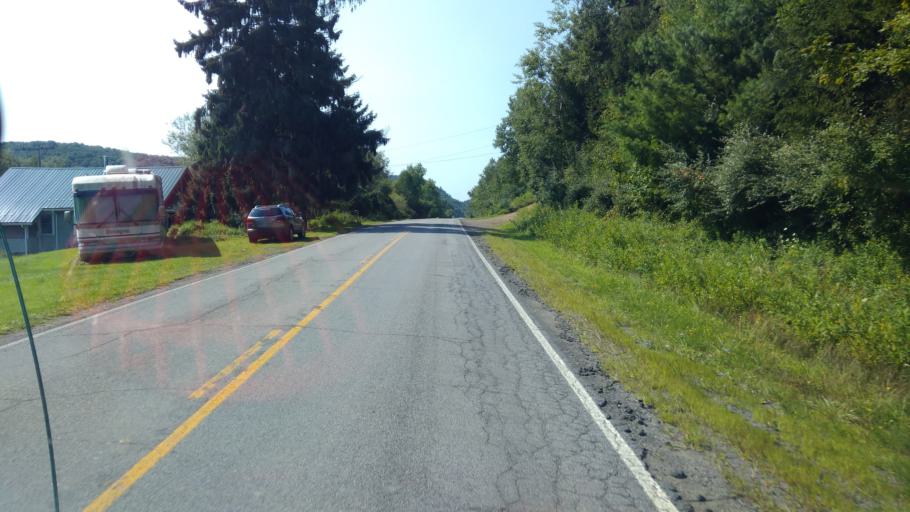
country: US
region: New York
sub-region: Allegany County
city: Bolivar
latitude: 42.1351
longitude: -78.1515
